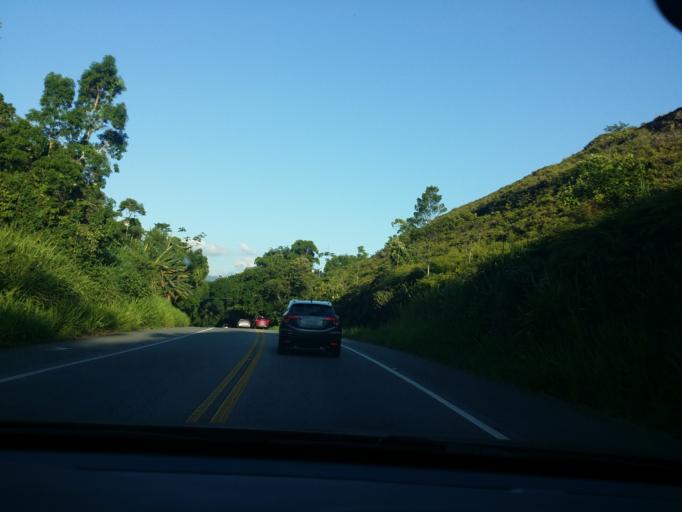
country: BR
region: Sao Paulo
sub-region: Sao Sebastiao
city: Sao Sebastiao
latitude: -23.7710
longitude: -45.7043
